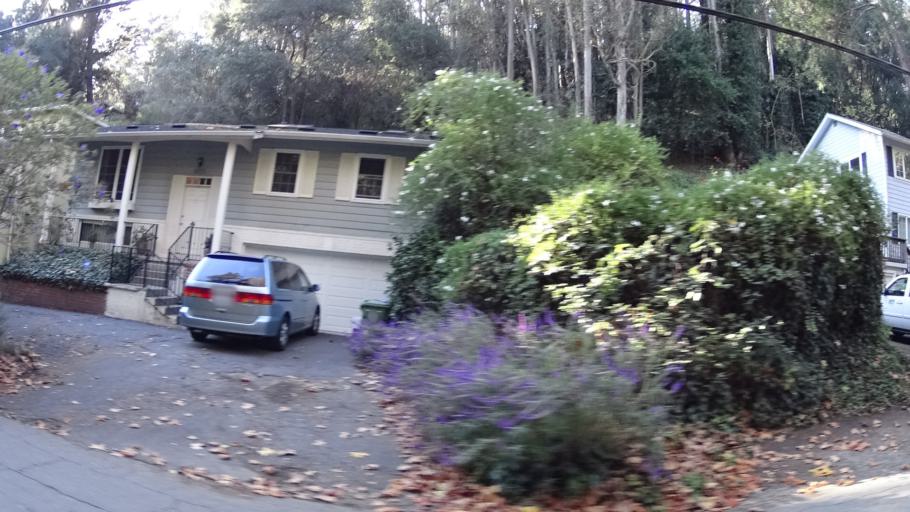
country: US
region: California
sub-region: Alameda County
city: Piedmont
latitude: 37.8429
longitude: -122.2090
